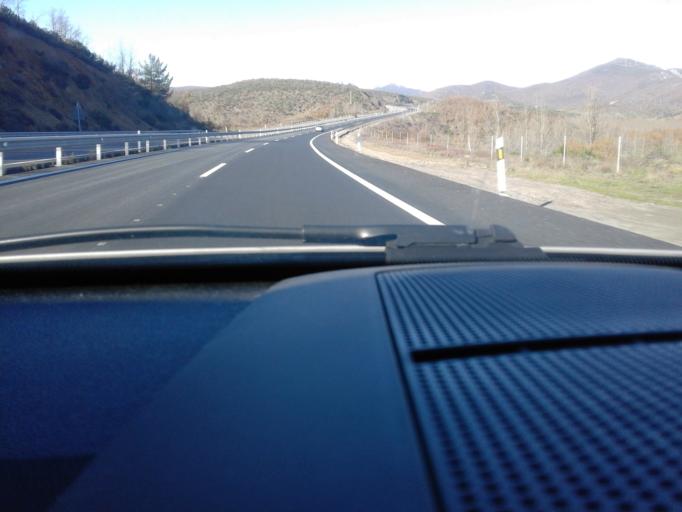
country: ES
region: Castille and Leon
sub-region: Provincia de Leon
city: Santa Maria de Ordas
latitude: 42.7919
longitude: -5.8196
